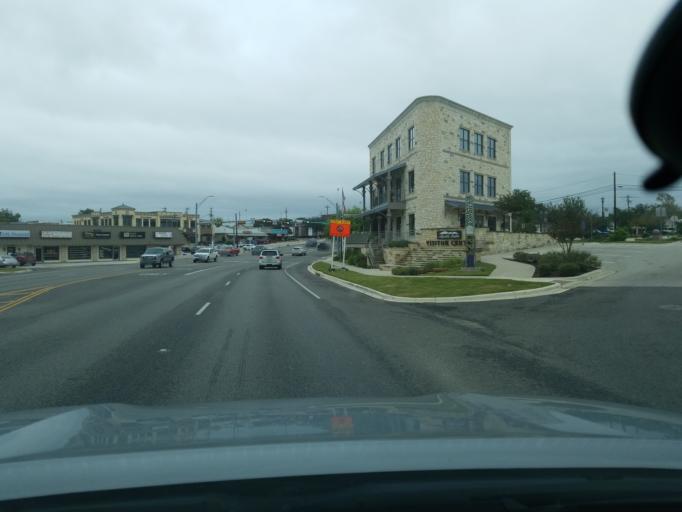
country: US
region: Texas
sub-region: Burnet County
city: Marble Falls
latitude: 30.5694
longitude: -98.2760
